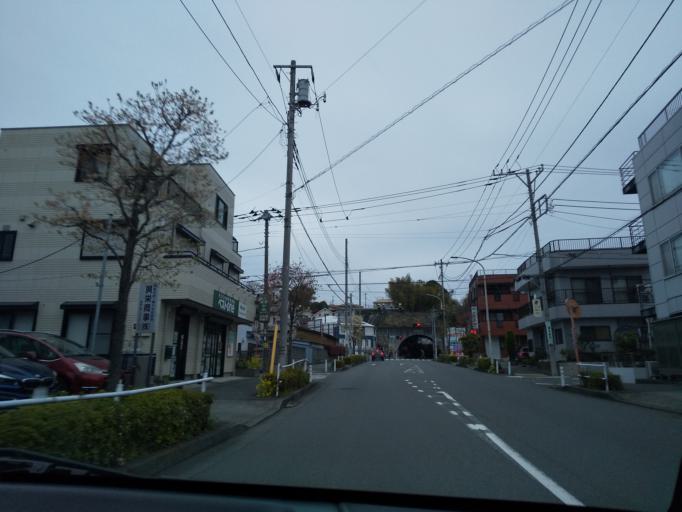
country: JP
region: Tokyo
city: Hachioji
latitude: 35.6020
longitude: 139.3485
